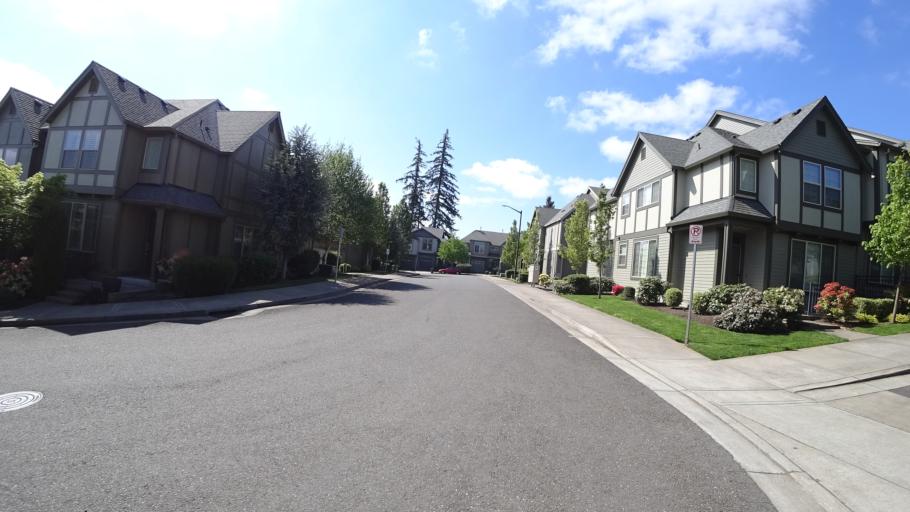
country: US
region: Oregon
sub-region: Washington County
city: King City
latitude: 45.4337
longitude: -122.8334
